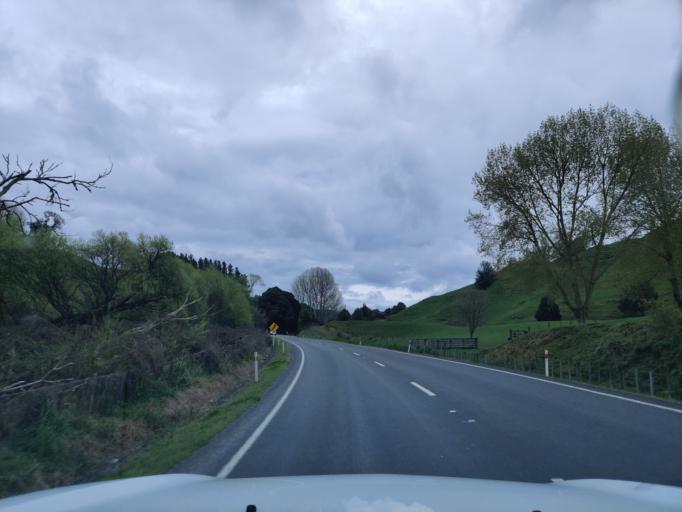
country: NZ
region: Waikato
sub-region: Otorohanga District
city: Otorohanga
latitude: -38.4858
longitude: 175.1837
